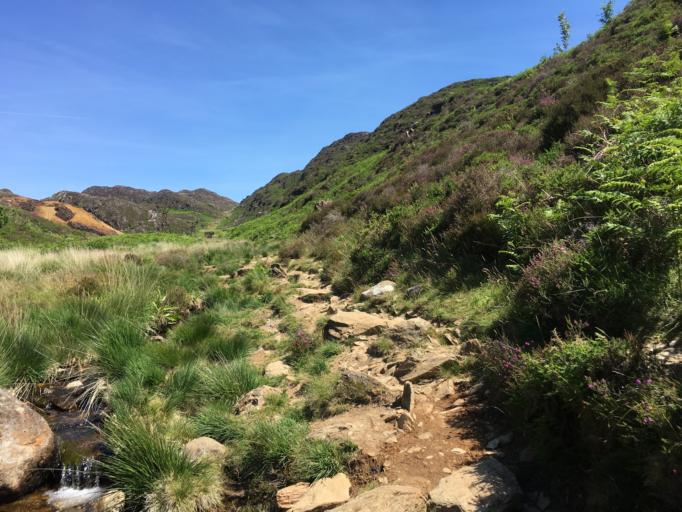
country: GB
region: Wales
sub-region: Gwynedd
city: Penrhyndeudraeth
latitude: 53.0056
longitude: -4.0828
